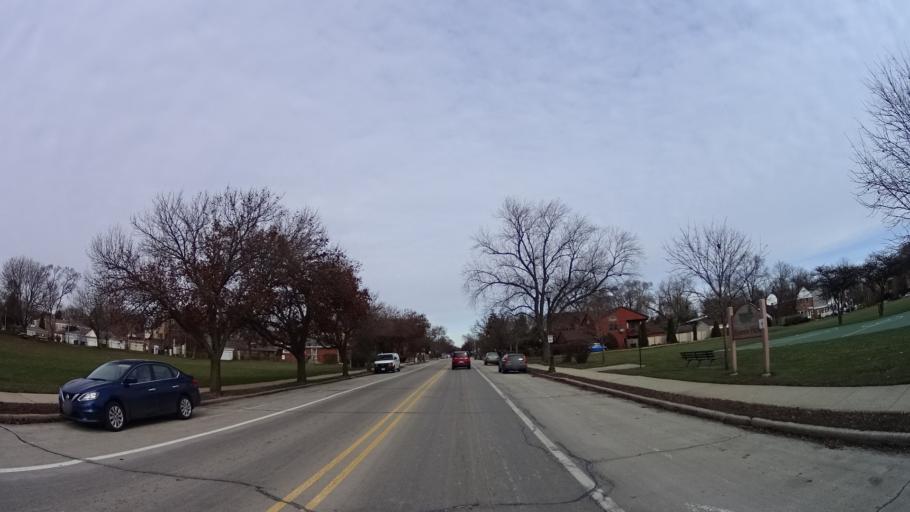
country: US
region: Illinois
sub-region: Cook County
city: Evanston
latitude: 42.0279
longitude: -87.6900
